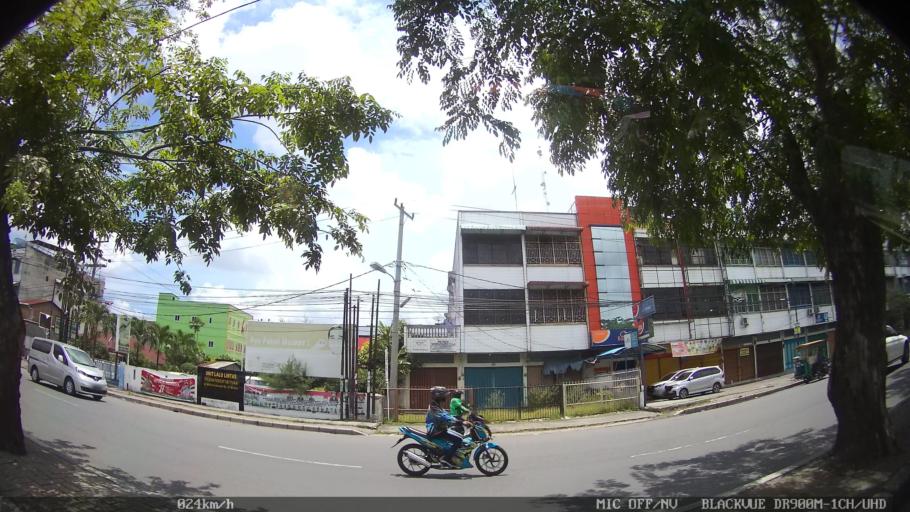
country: ID
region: North Sumatra
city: Medan
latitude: 3.5991
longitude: 98.7063
